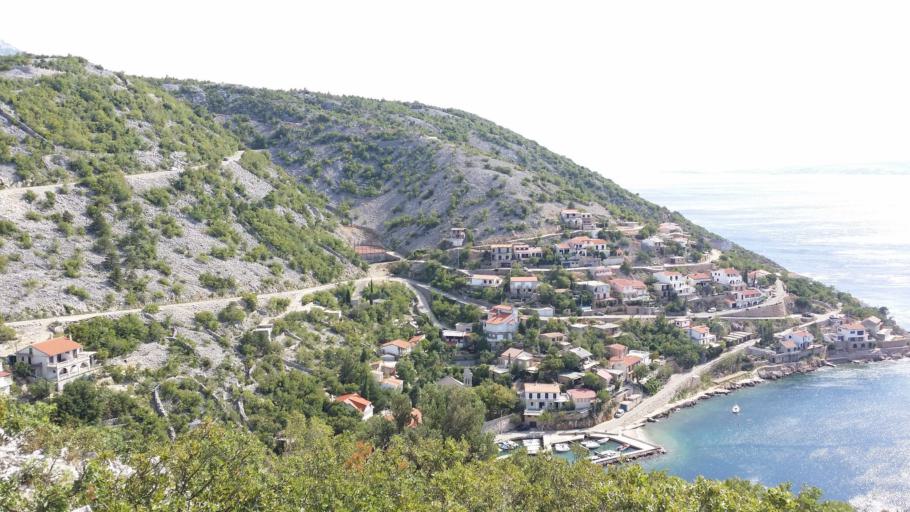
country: HR
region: Primorsko-Goranska
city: Banjol
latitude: 44.8000
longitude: 14.8813
